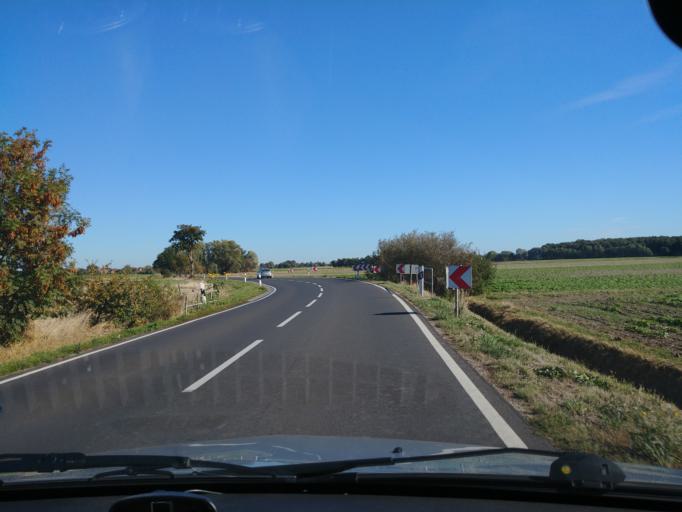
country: DE
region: Lower Saxony
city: Leiferde
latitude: 52.4248
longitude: 10.4264
